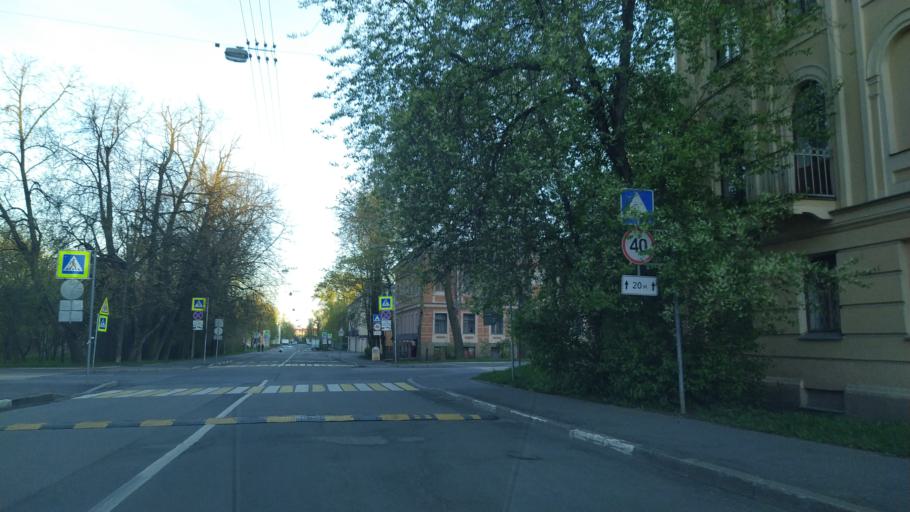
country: RU
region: St.-Petersburg
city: Pushkin
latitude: 59.7081
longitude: 30.4088
